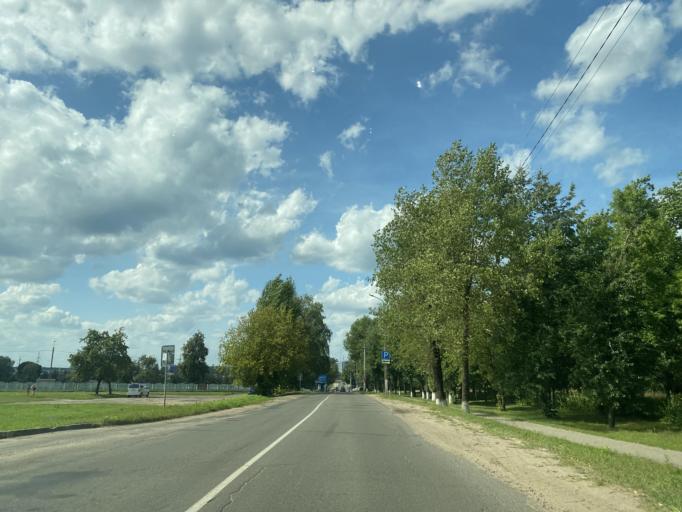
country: BY
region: Minsk
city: Horad Zhodzina
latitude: 54.0983
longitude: 28.3539
